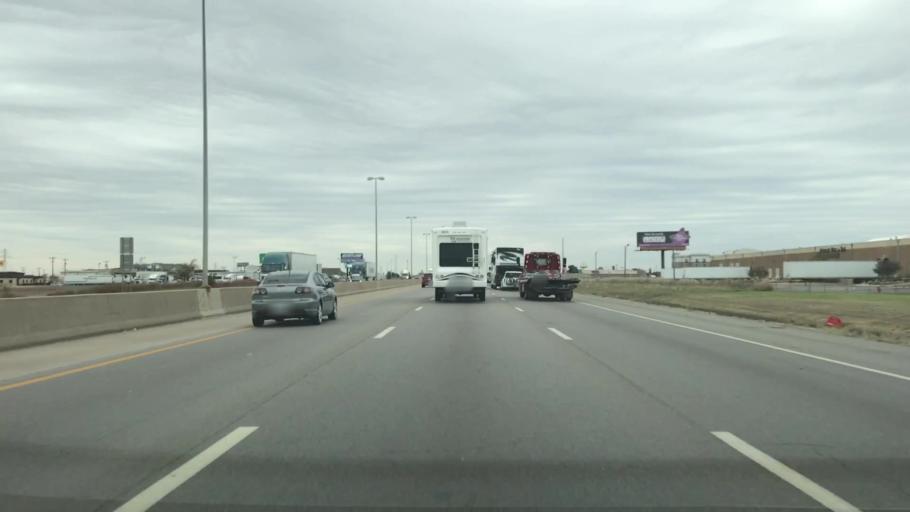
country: US
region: Oklahoma
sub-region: Oklahoma County
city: Bethany
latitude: 35.4602
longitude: -97.6112
